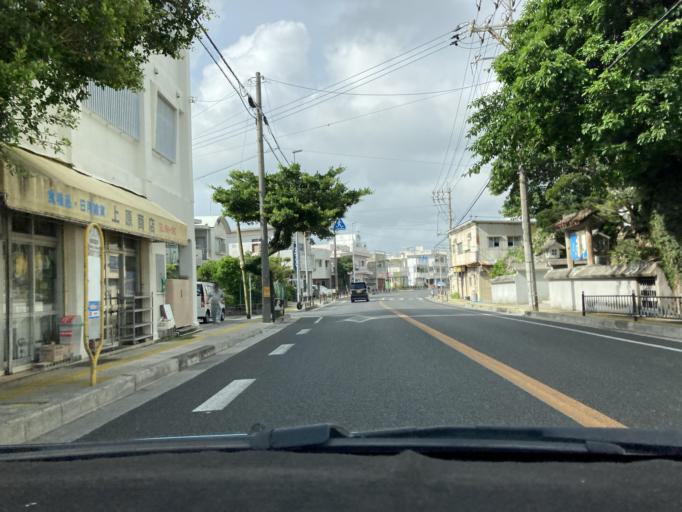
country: JP
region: Okinawa
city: Itoman
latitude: 26.1333
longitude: 127.6700
